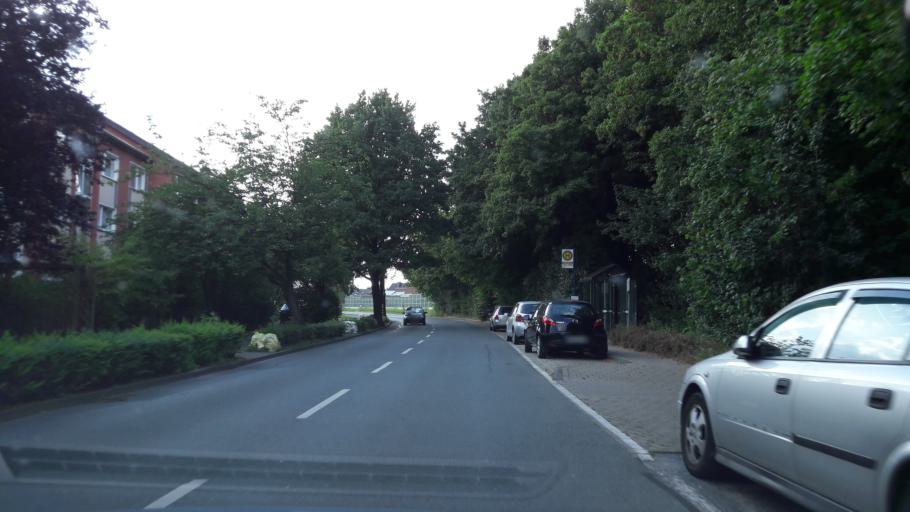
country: DE
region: North Rhine-Westphalia
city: Sendenhorst
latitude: 51.8481
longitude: 7.8250
